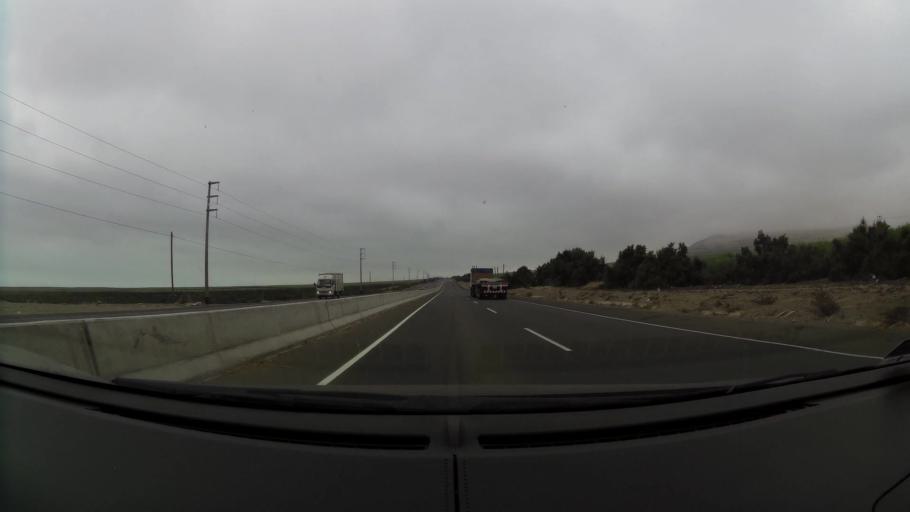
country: PE
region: La Libertad
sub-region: Provincia de Trujillo
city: Salaverry
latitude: -8.3336
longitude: -78.8915
